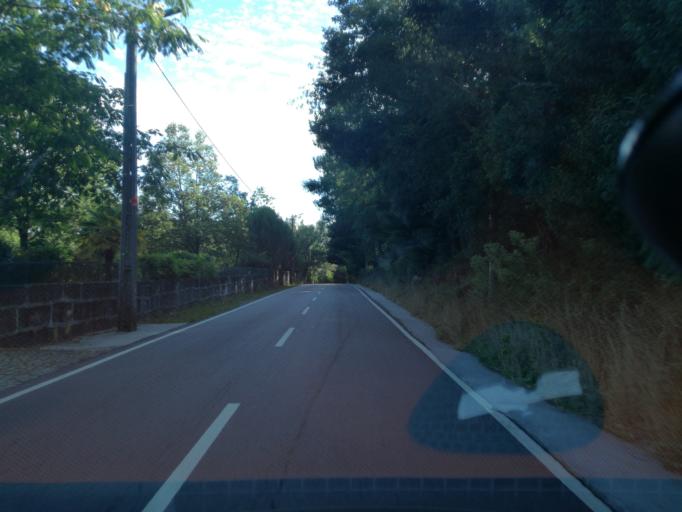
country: PT
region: Porto
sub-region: Santo Tirso
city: Sao Miguel do Couto
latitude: 41.3112
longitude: -8.4440
